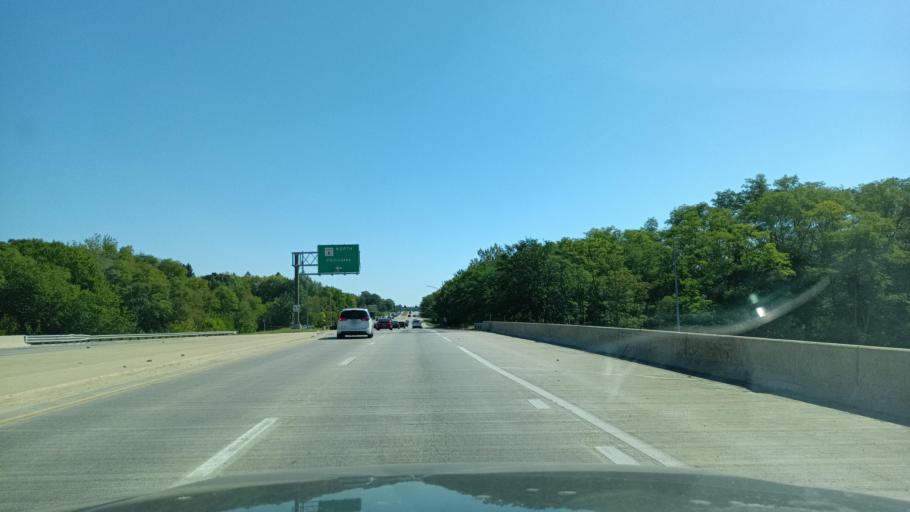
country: US
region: Illinois
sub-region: Peoria County
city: Dunlap
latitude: 40.7750
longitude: -89.6699
